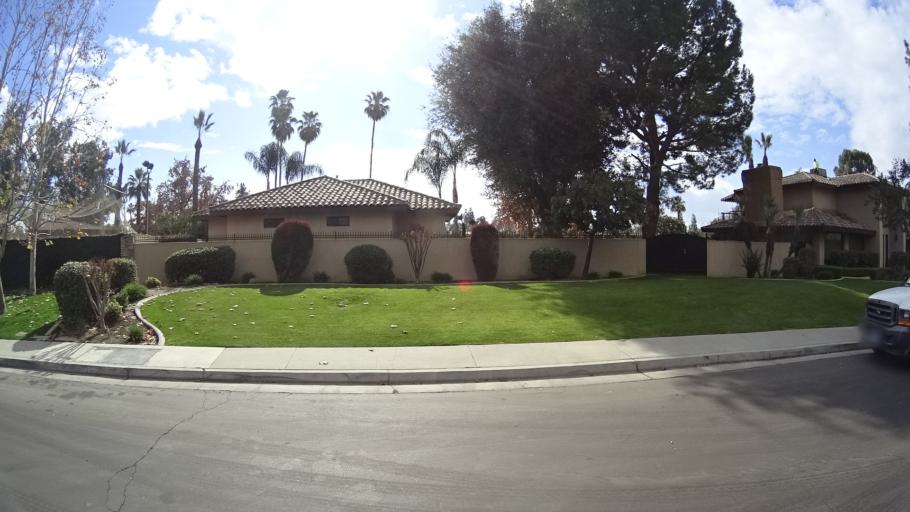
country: US
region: California
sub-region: Kern County
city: Greenacres
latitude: 35.3459
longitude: -119.0849
